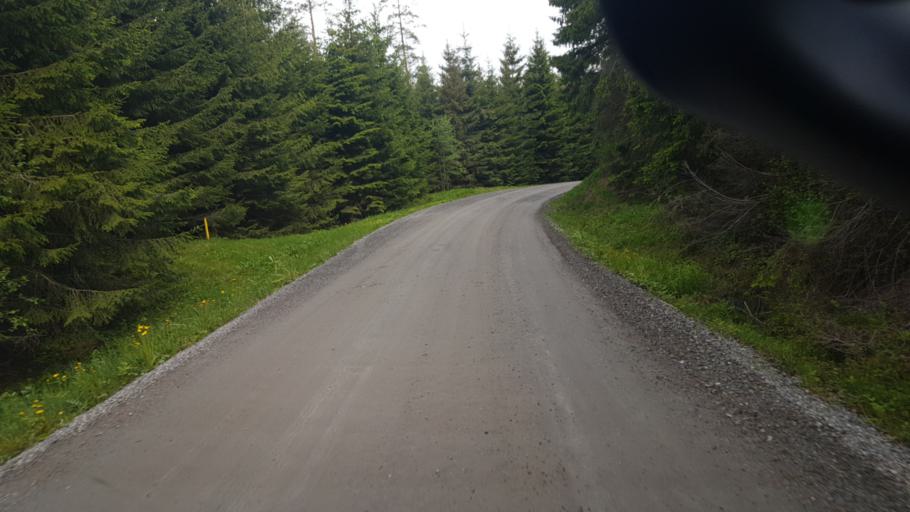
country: NO
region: Ostfold
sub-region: Romskog
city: Romskog
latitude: 59.6939
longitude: 11.9429
